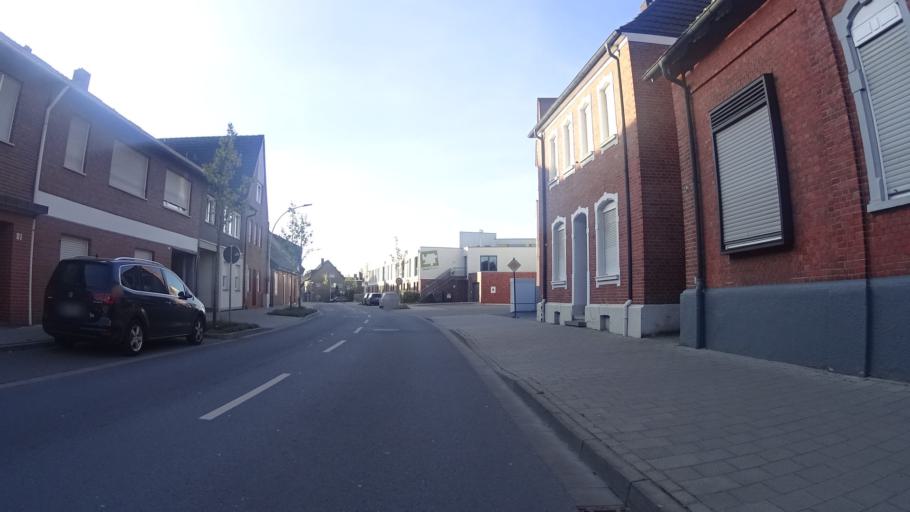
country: DE
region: North Rhine-Westphalia
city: Emsdetten
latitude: 52.1790
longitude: 7.5223
